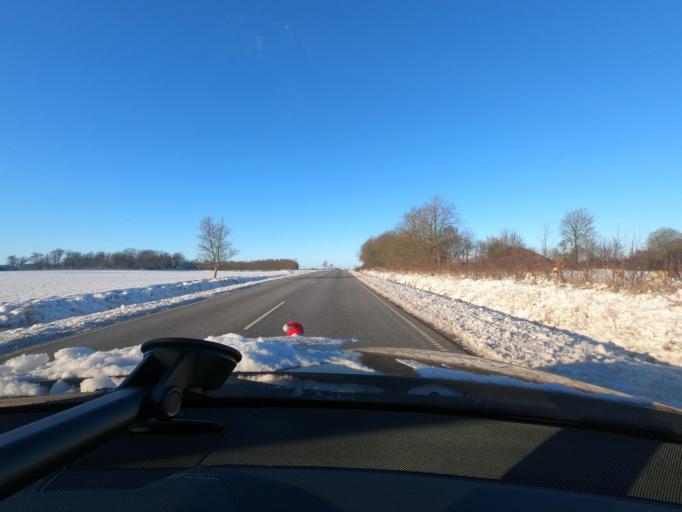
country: DK
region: South Denmark
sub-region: Tonder Kommune
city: Toftlund
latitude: 55.1203
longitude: 9.1556
